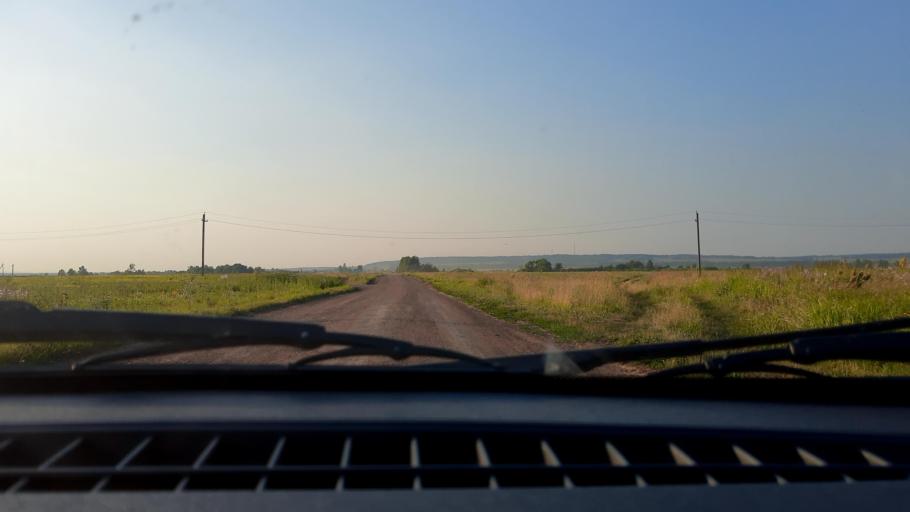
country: RU
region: Bashkortostan
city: Asanovo
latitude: 54.9344
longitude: 55.6236
